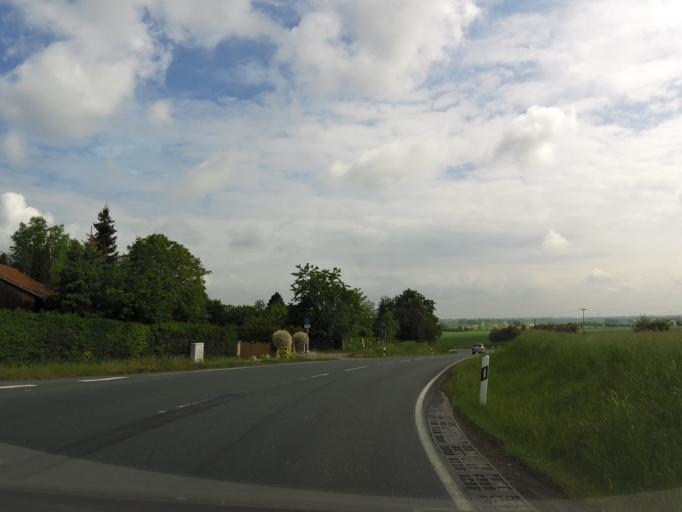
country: DE
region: Thuringia
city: Seebergen
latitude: 50.9115
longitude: 10.7997
